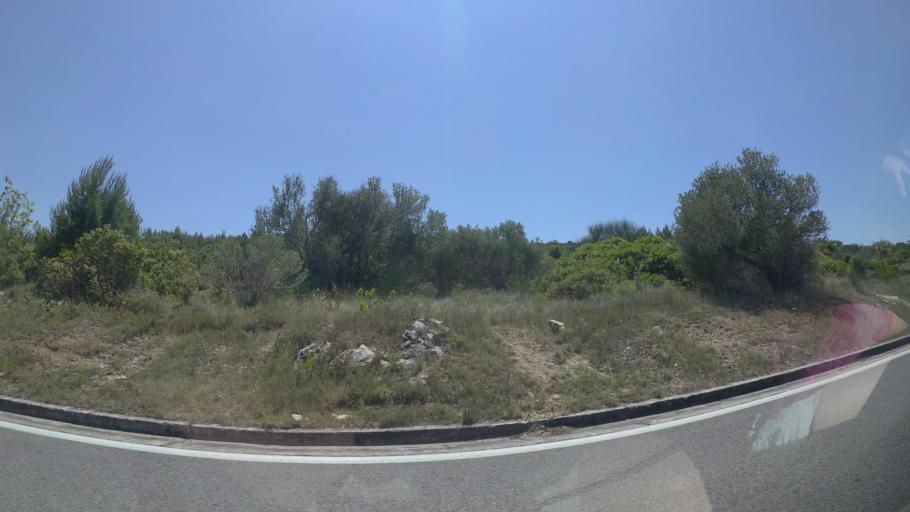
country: HR
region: Sibensko-Kniniska
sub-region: Grad Sibenik
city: Pirovac
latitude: 43.8046
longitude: 15.6681
